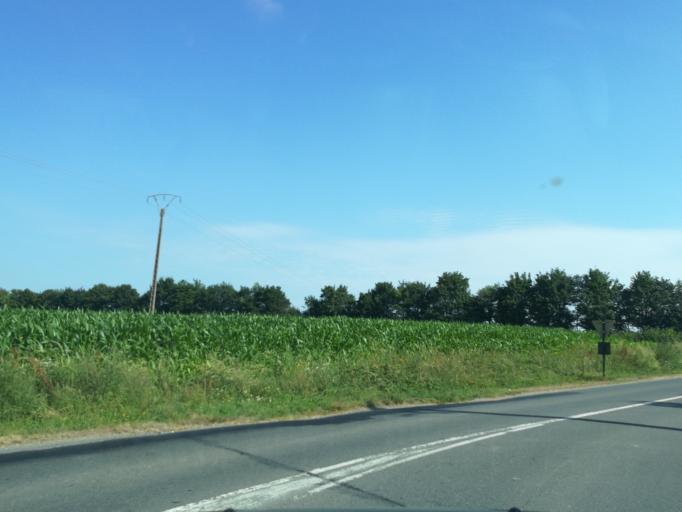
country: FR
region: Brittany
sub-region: Departement d'Ille-et-Vilaine
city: Montfort-sur-Meu
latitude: 48.1494
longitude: -1.9474
